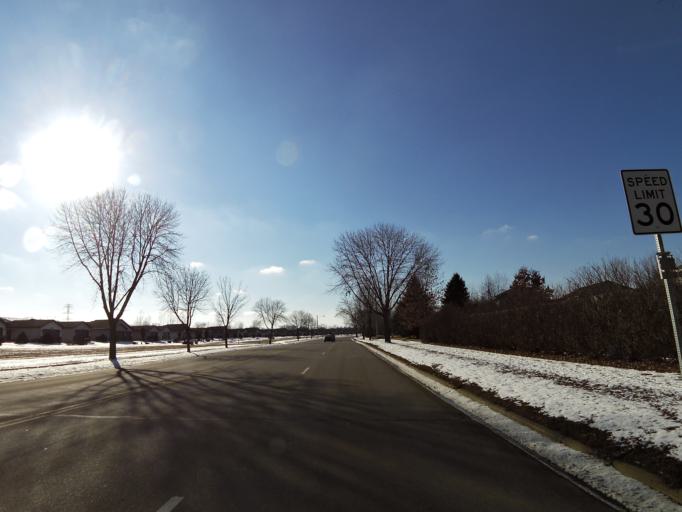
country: US
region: Minnesota
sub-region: Scott County
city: Shakopee
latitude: 44.7810
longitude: -93.4933
